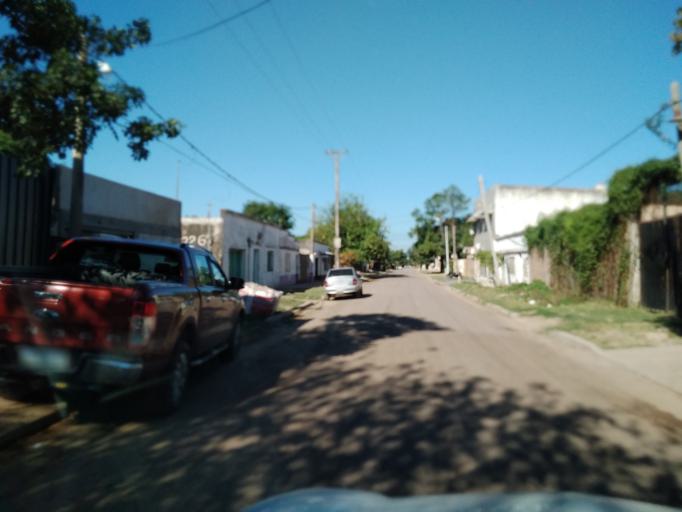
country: AR
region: Corrientes
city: Corrientes
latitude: -27.4835
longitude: -58.8122
